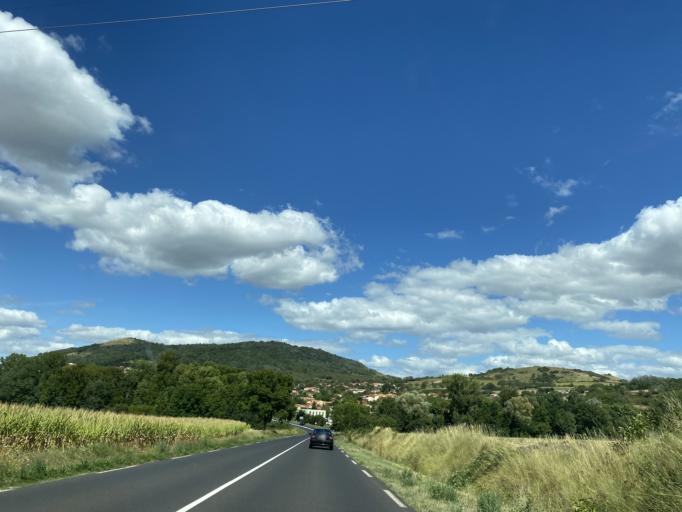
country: FR
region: Auvergne
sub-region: Departement du Puy-de-Dome
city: Mezel
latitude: 45.7461
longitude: 3.2370
